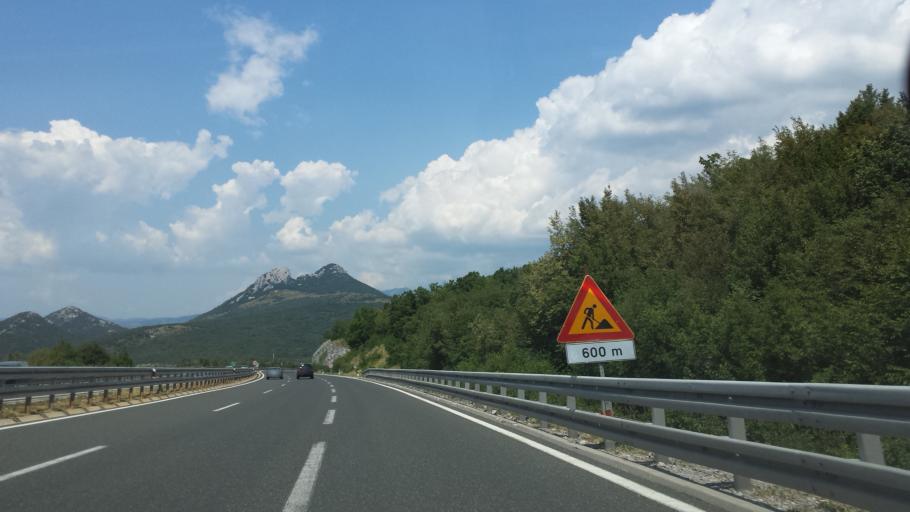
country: HR
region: Primorsko-Goranska
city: Krasica
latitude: 45.3535
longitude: 14.5820
